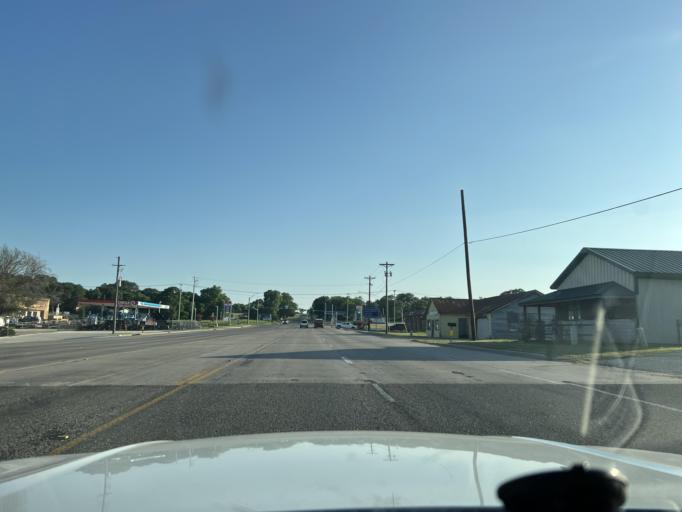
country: US
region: Texas
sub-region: Washington County
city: Brenham
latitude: 30.1795
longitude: -96.3835
